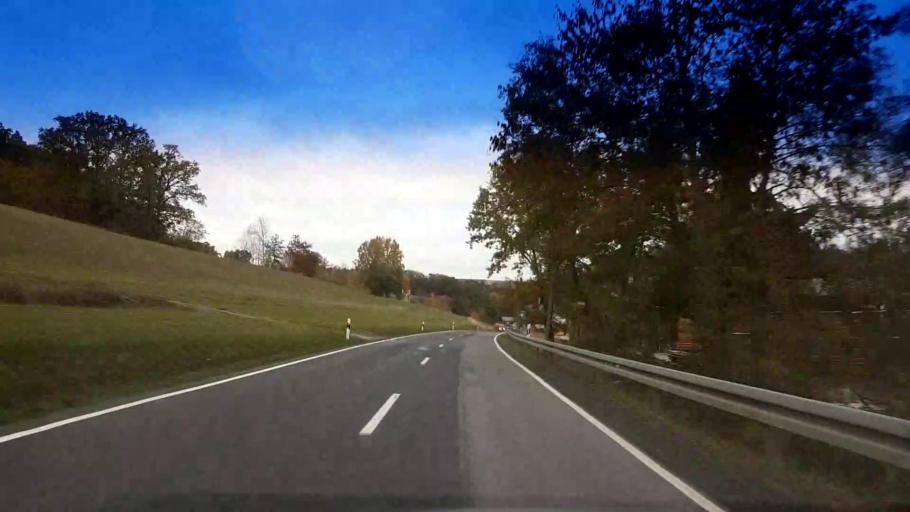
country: DE
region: Bavaria
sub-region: Regierungsbezirk Unterfranken
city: Stettfeld
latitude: 49.9470
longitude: 10.7050
